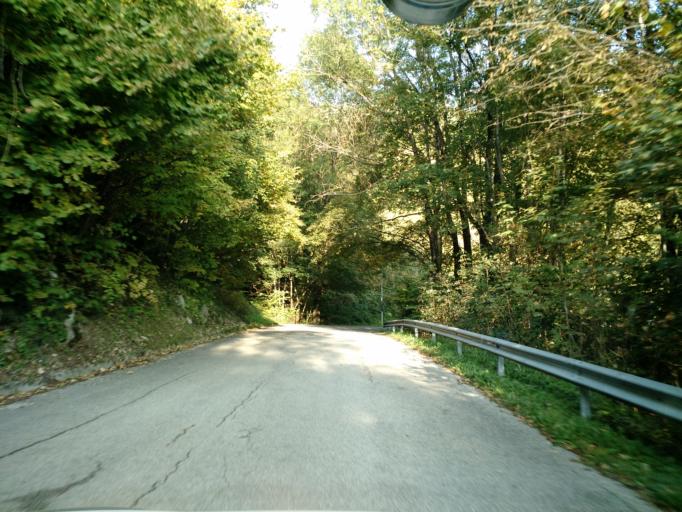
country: IT
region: Veneto
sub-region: Provincia di Vicenza
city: Foza
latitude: 45.8664
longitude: 11.6178
